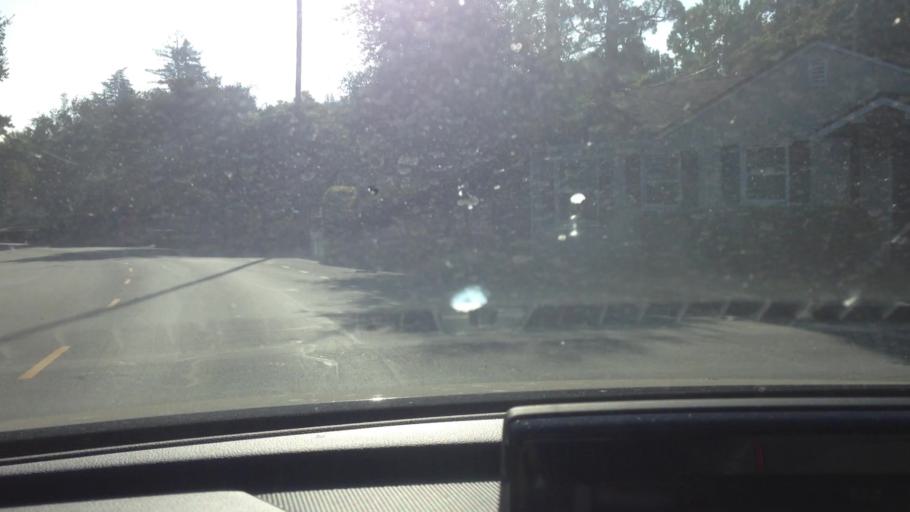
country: US
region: California
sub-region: Santa Clara County
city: Saratoga
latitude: 37.2596
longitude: -122.0303
